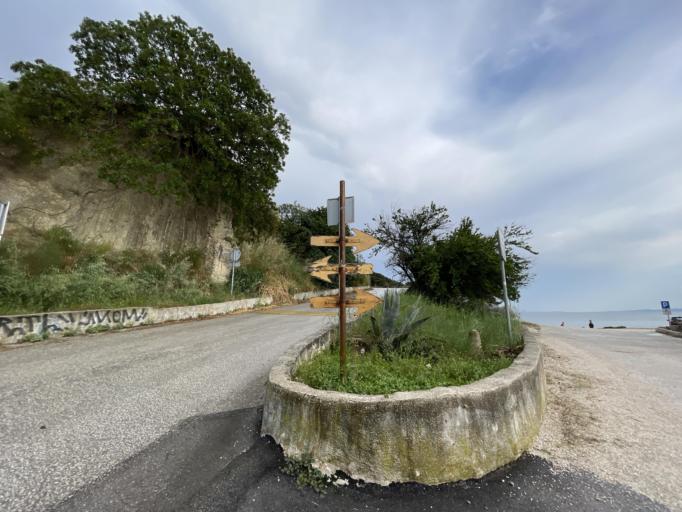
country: HR
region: Splitsko-Dalmatinska
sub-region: Grad Split
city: Split
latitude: 43.5054
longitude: 16.4011
